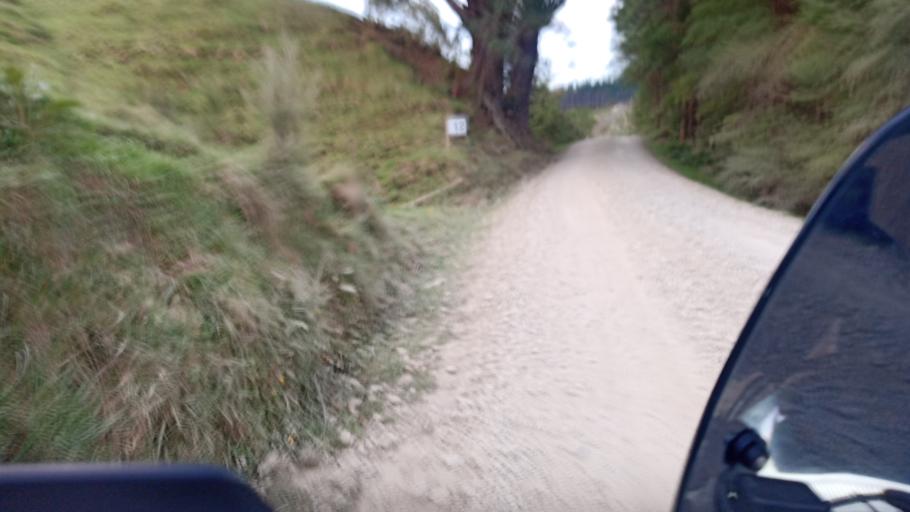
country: NZ
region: Gisborne
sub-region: Gisborne District
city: Gisborne
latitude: -38.4692
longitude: 177.9761
